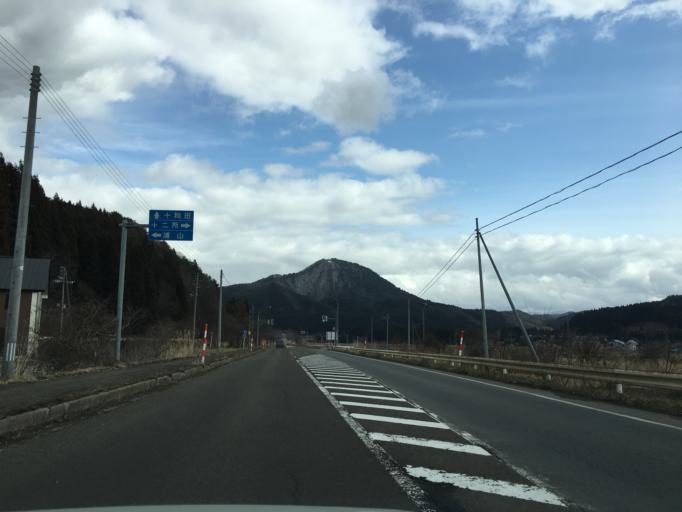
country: JP
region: Akita
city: Odate
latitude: 40.2221
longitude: 140.6644
